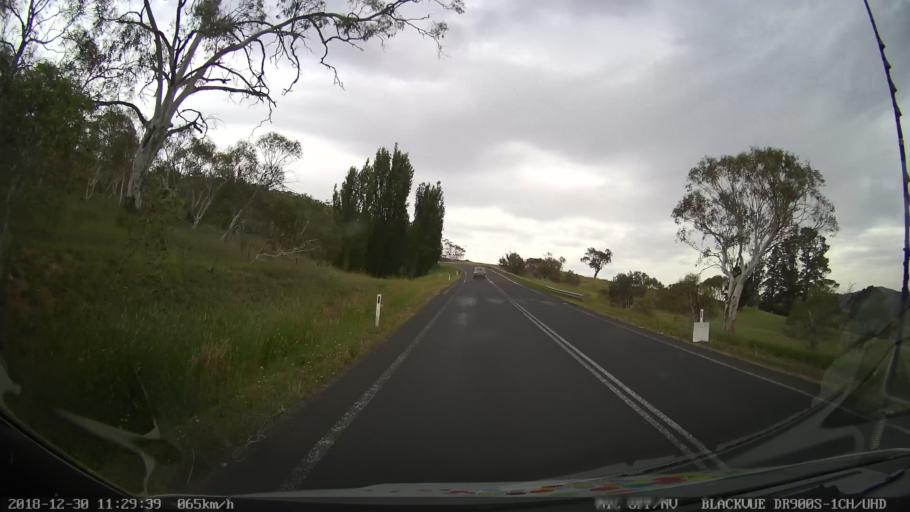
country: AU
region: New South Wales
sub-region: Snowy River
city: Jindabyne
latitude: -36.4486
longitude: 148.6094
